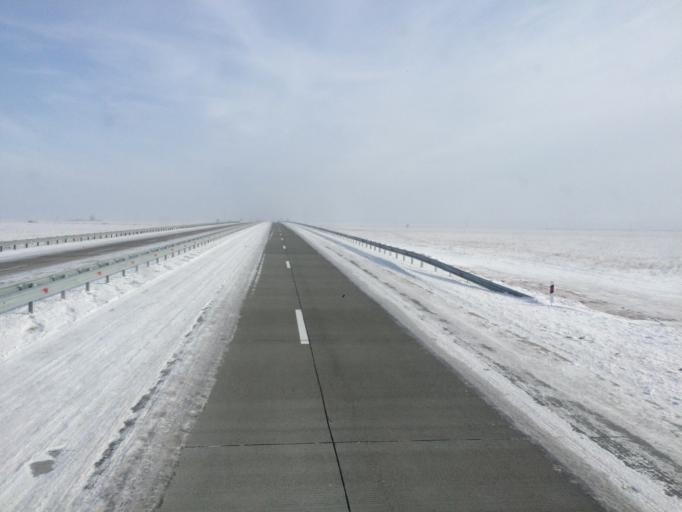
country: KZ
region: Zhambyl
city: Georgiyevka
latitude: 43.3425
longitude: 74.4011
